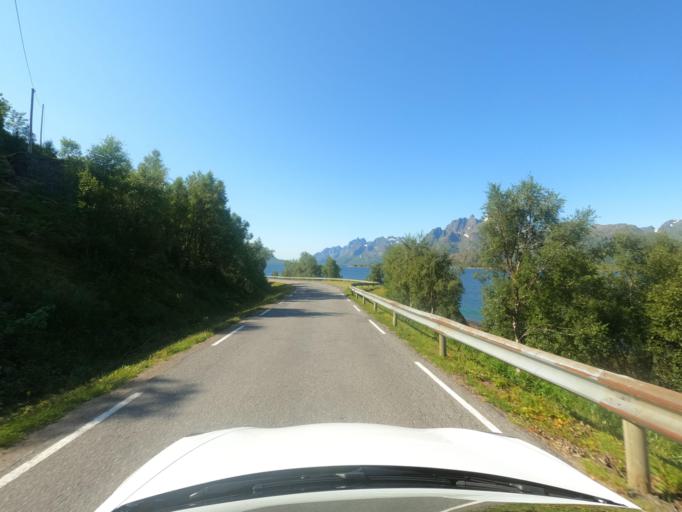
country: NO
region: Nordland
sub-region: Hadsel
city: Stokmarknes
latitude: 68.3463
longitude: 15.0532
